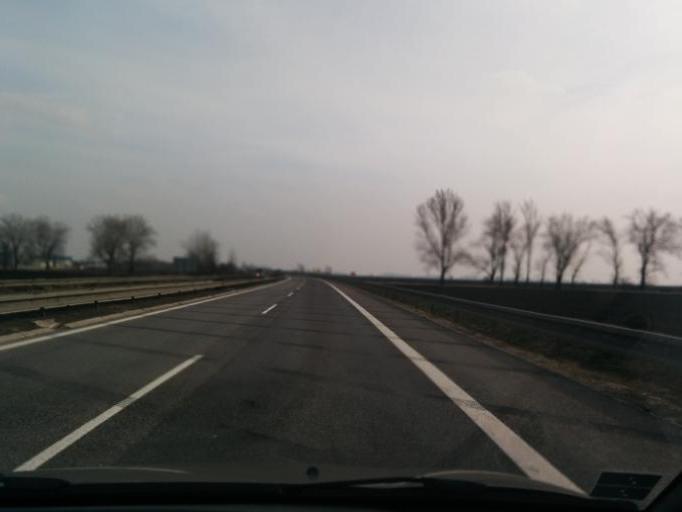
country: SK
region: Trnavsky
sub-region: Okres Galanta
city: Galanta
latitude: 48.2607
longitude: 17.7354
